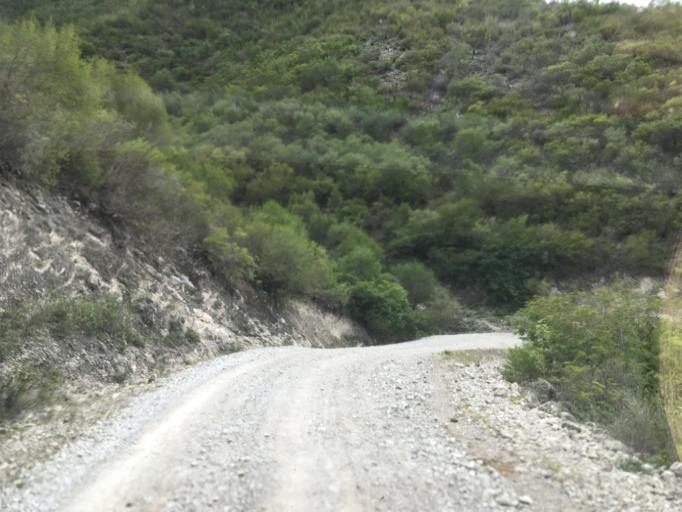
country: MX
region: Hidalgo
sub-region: Metztitlan
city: Fontezuelas
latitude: 20.6235
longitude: -98.8782
